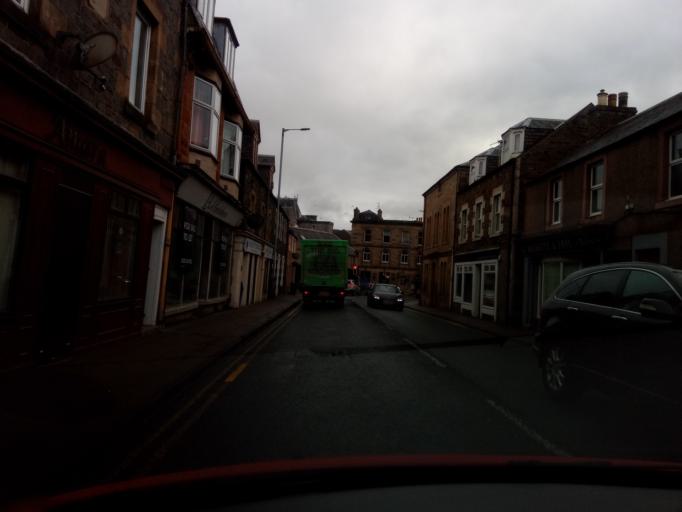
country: GB
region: Scotland
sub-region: The Scottish Borders
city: Galashiels
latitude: 55.6194
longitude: -2.8129
